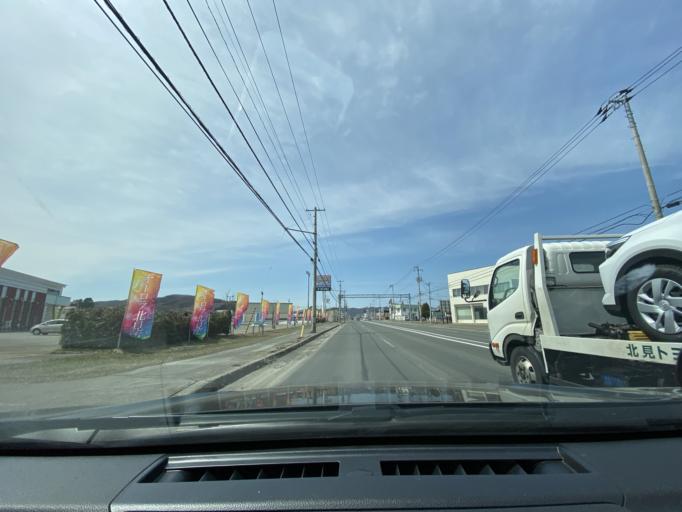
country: JP
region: Hokkaido
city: Kitami
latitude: 43.7979
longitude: 143.8340
